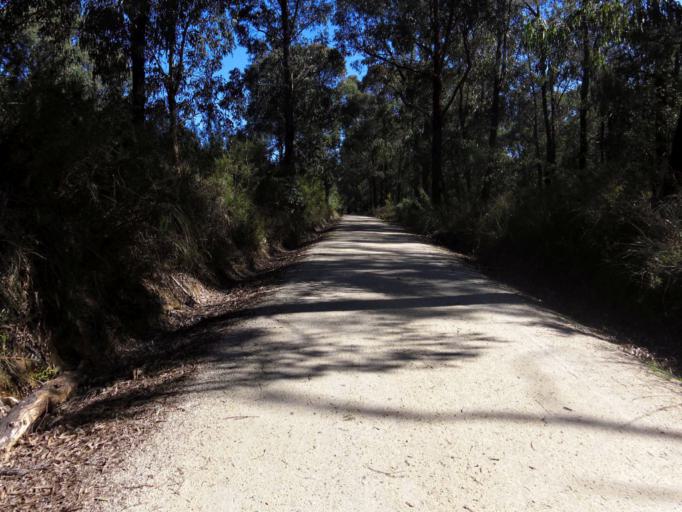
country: AU
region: Victoria
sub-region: Latrobe
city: Moe
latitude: -38.3752
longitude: 146.1980
